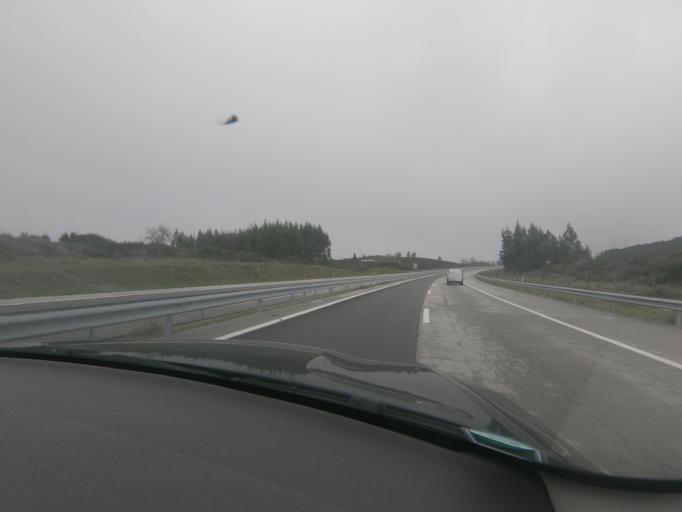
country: PT
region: Viseu
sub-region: Castro Daire
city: Castro Daire
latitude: 40.9537
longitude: -7.8922
